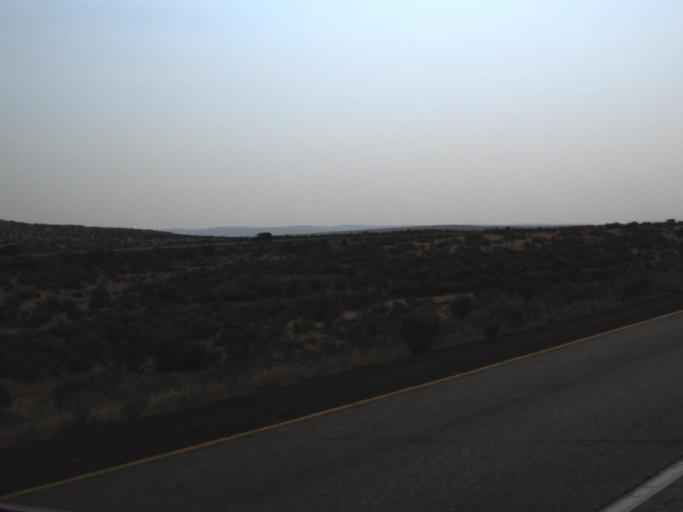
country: US
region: Washington
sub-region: Kittitas County
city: Kittitas
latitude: 46.8198
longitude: -120.3588
